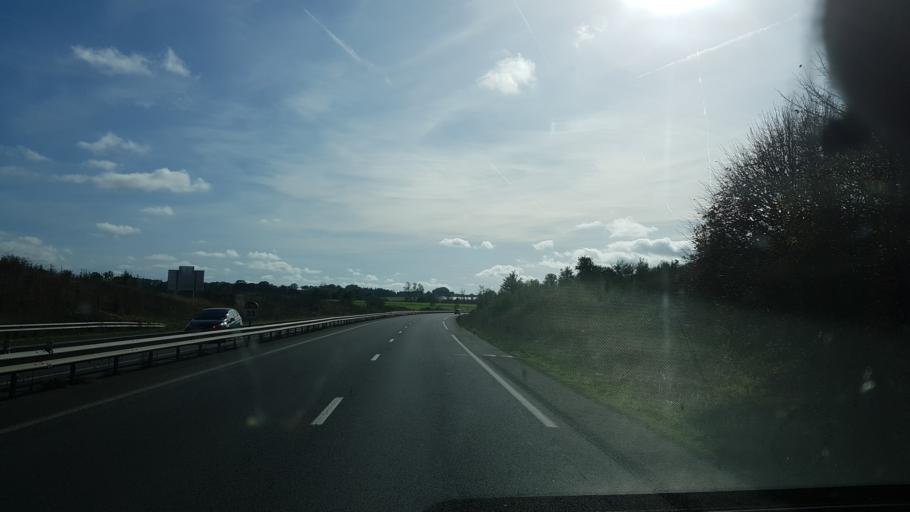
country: FR
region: Poitou-Charentes
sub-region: Departement de la Charente
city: Chasseneuil-sur-Bonnieure
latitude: 45.8210
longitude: 0.4568
